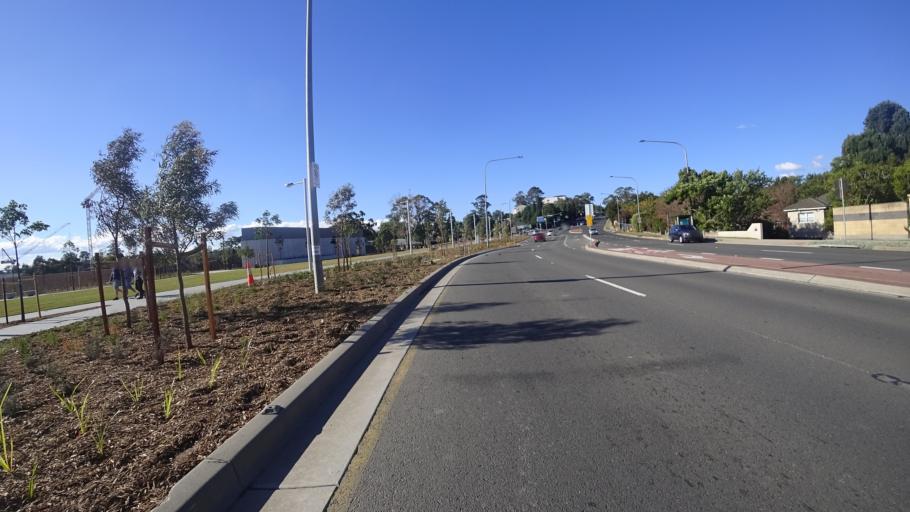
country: AU
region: New South Wales
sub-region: The Hills Shire
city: Castle Hill
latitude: -33.7316
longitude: 151.0082
